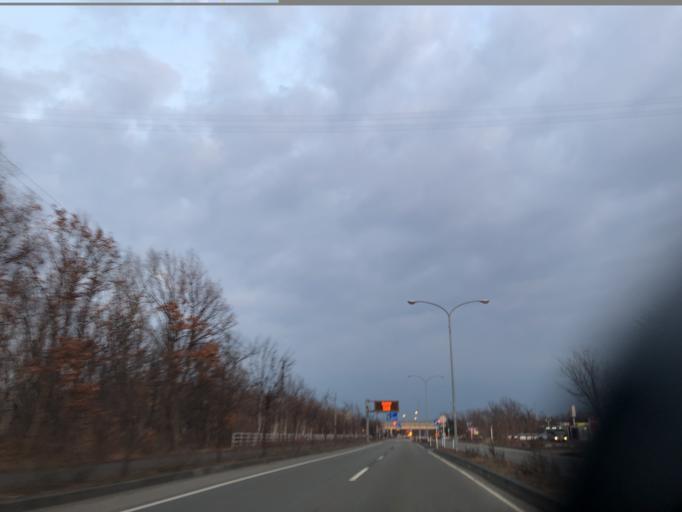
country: JP
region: Hokkaido
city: Chitose
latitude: 42.8194
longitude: 141.6782
